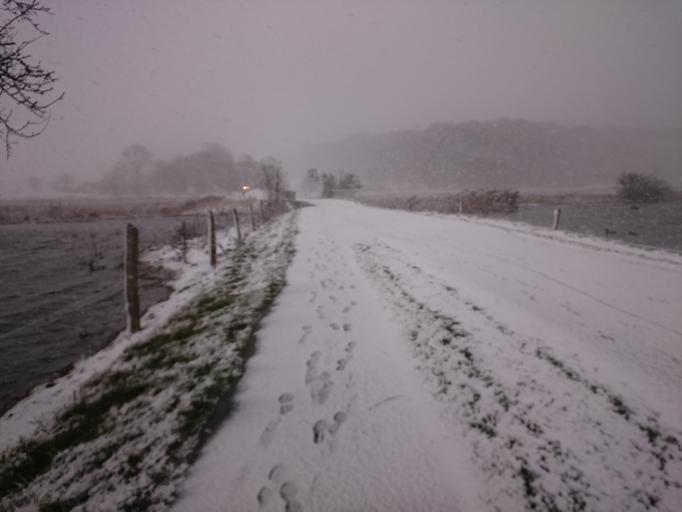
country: DK
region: Central Jutland
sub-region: Arhus Kommune
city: Stavtrup
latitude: 56.1340
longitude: 10.1336
